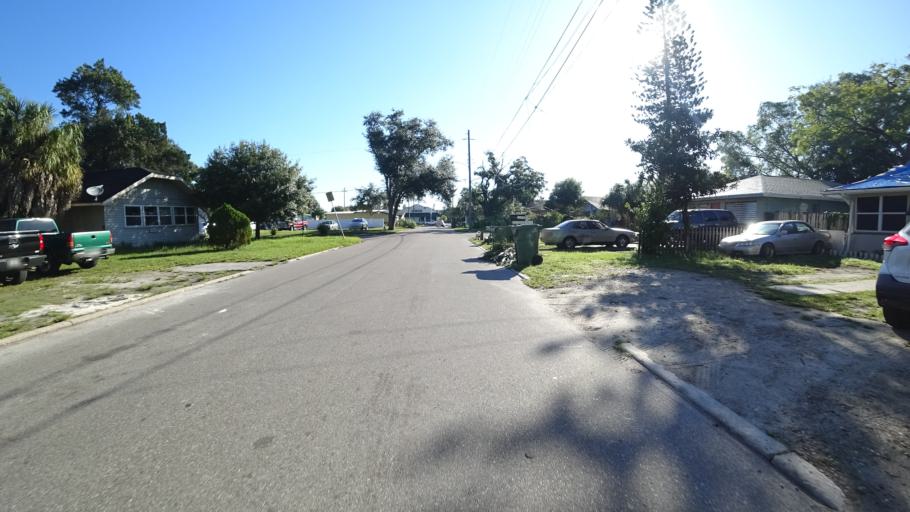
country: US
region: Florida
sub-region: Manatee County
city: West Samoset
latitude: 27.4789
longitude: -82.5724
